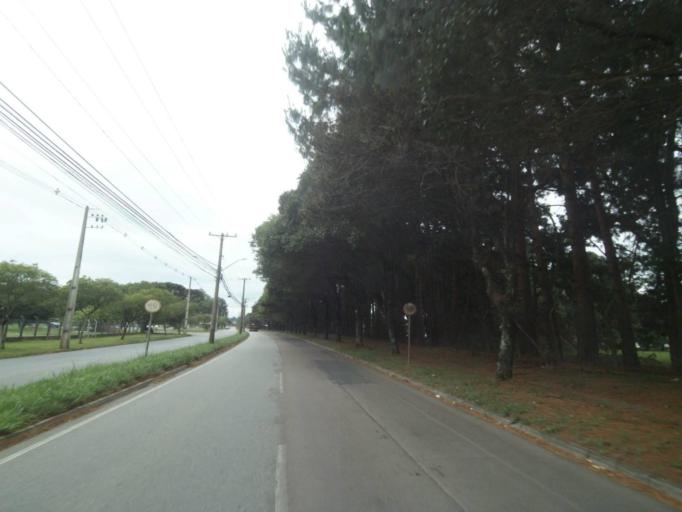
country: BR
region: Parana
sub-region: Sao Jose Dos Pinhais
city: Sao Jose dos Pinhais
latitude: -25.5503
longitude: -49.3125
